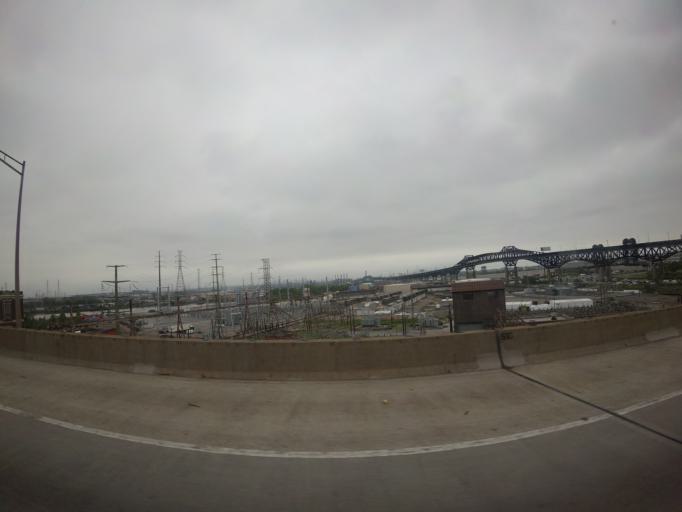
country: US
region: New Jersey
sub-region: Hudson County
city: Harrison
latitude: 40.7377
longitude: -74.1237
